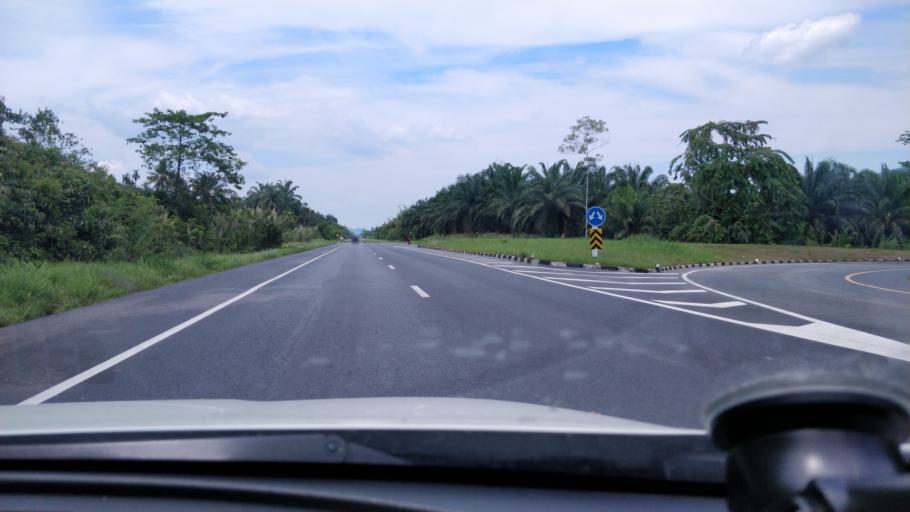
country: TH
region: Krabi
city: Plai Phraya
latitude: 8.4942
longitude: 98.8798
